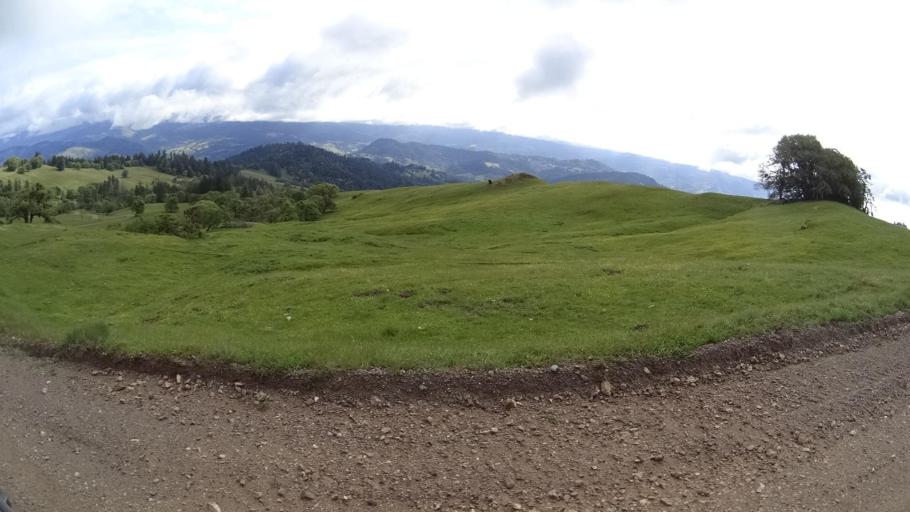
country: US
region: California
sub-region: Humboldt County
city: Redway
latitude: 40.2018
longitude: -123.6938
